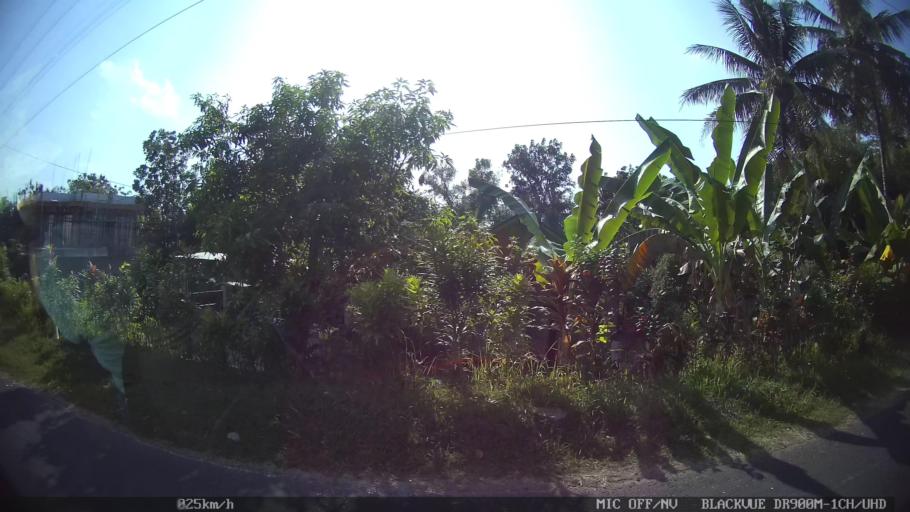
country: ID
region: Daerah Istimewa Yogyakarta
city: Kasihan
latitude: -7.8292
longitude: 110.2883
